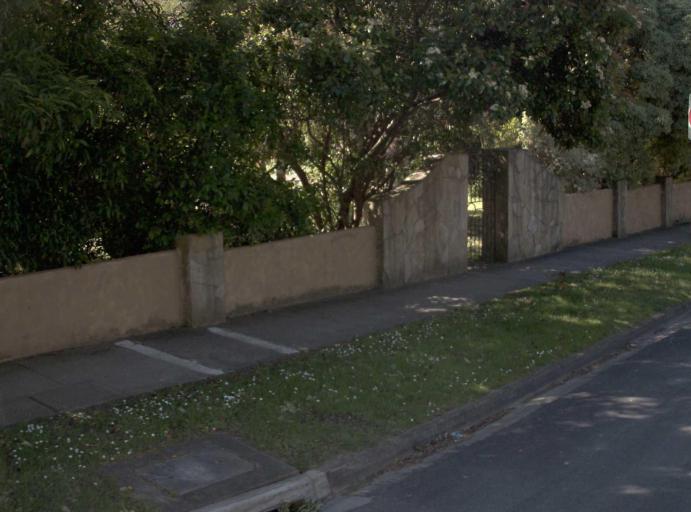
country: AU
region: Victoria
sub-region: Maroondah
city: Croydon South
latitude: -37.7972
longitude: 145.2770
